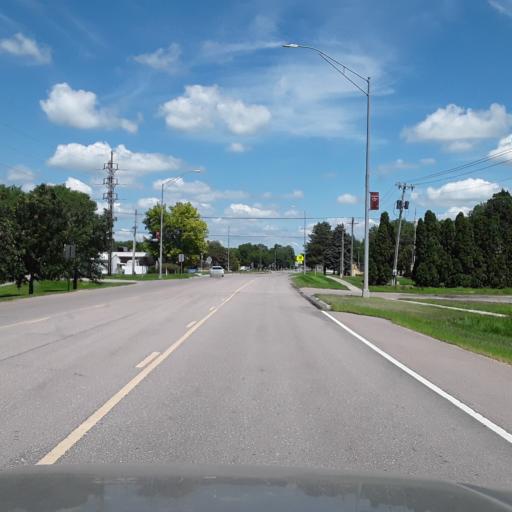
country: US
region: Nebraska
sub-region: Merrick County
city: Central City
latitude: 41.1037
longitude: -98.0017
